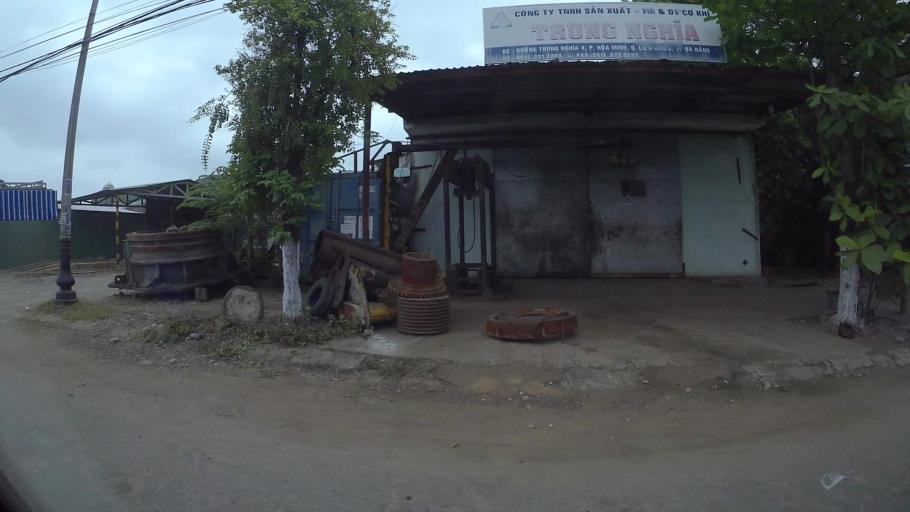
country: VN
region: Da Nang
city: Thanh Khe
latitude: 16.0629
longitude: 108.1744
